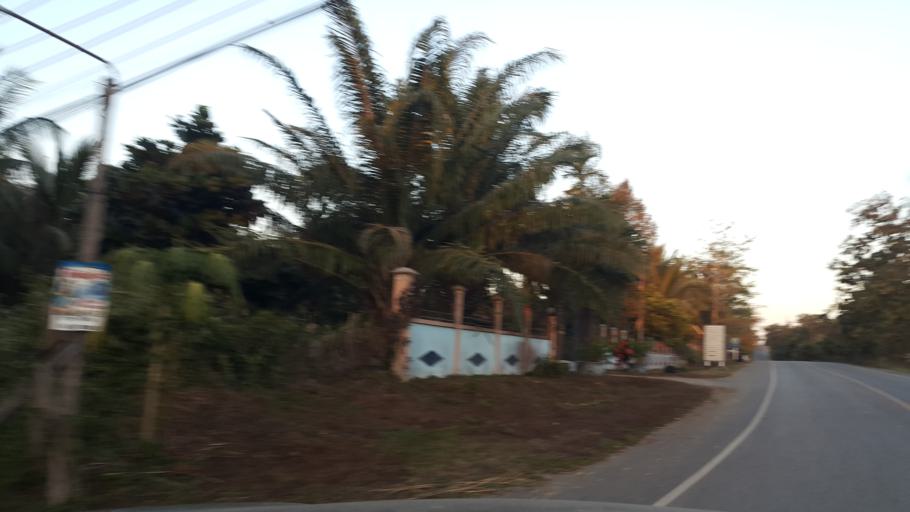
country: TH
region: Phrae
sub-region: Amphoe Wang Chin
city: Wang Chin
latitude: 17.8797
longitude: 99.6198
